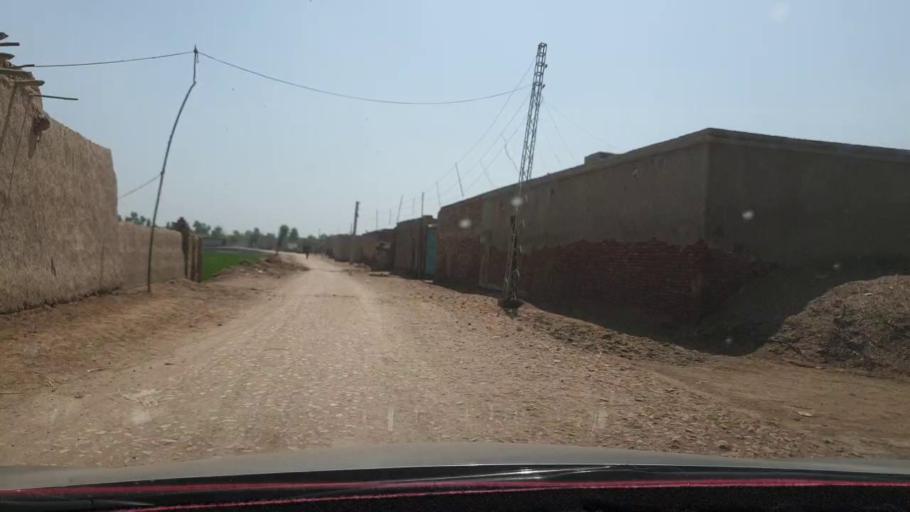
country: PK
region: Sindh
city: Warah
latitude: 27.4851
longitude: 67.8238
